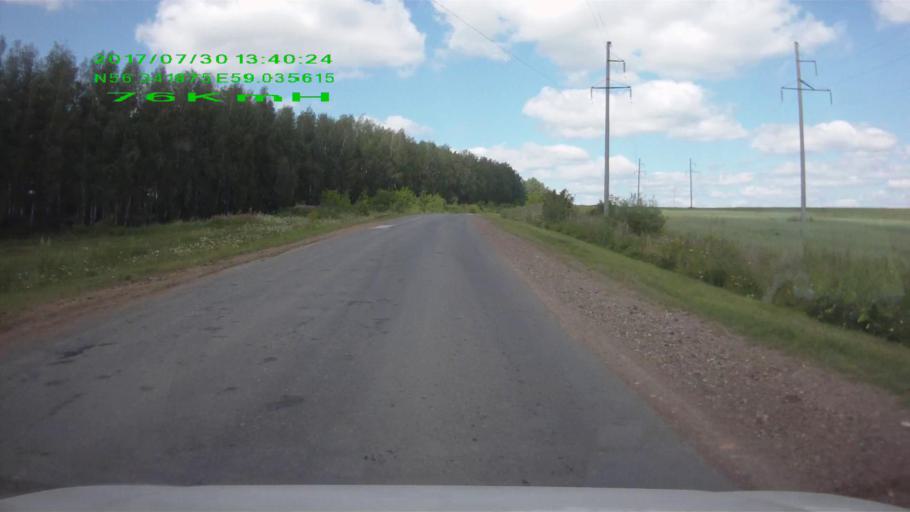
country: RU
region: Sverdlovsk
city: Mikhaylovsk
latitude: 56.3423
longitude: 59.0355
